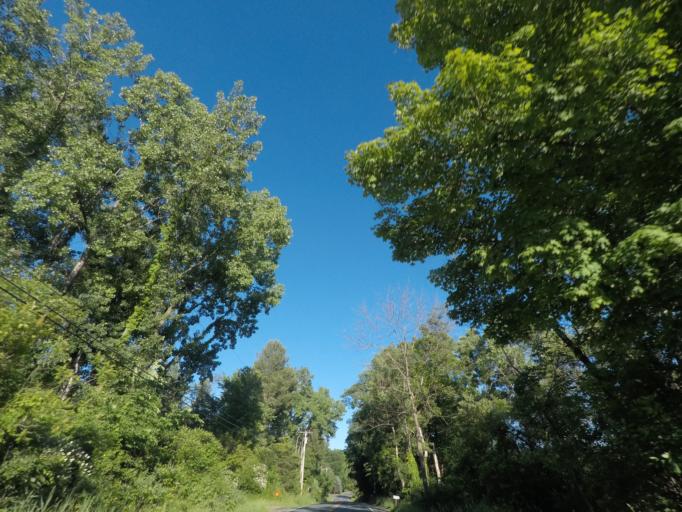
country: US
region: New York
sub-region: Rensselaer County
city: Averill Park
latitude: 42.5926
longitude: -73.5866
